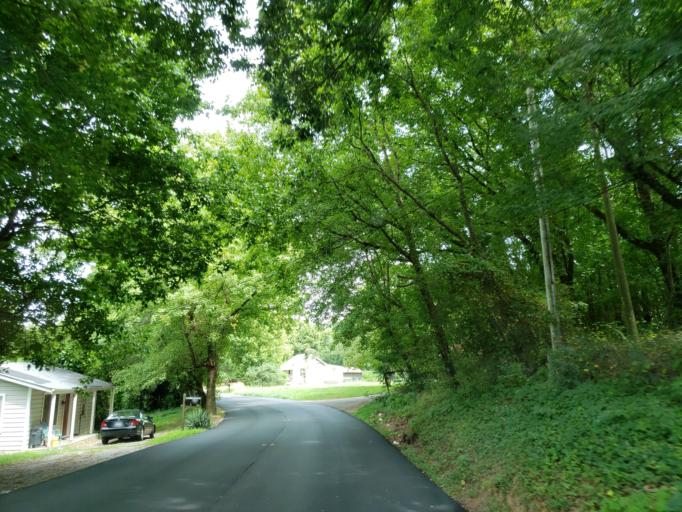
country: US
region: Georgia
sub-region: Pickens County
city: Jasper
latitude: 34.4529
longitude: -84.4439
